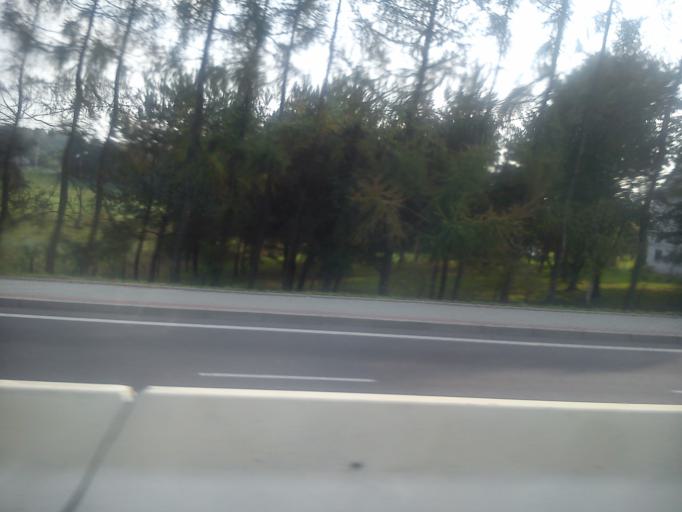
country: PL
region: Subcarpathian Voivodeship
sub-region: Powiat lancucki
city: Lancut
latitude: 50.0598
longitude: 22.2133
